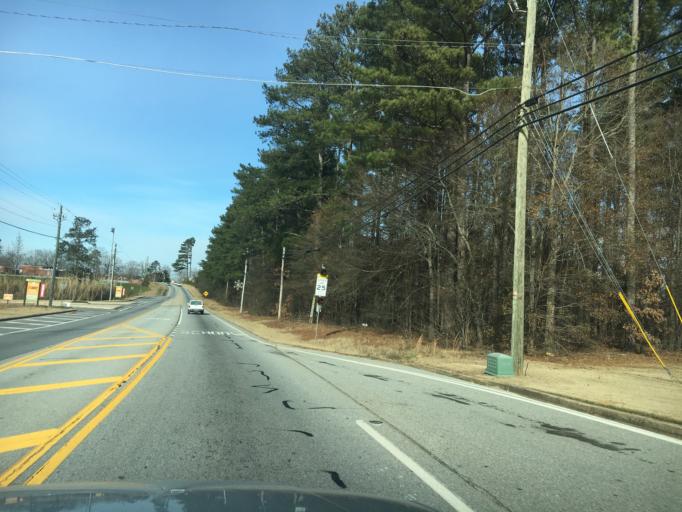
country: US
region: Georgia
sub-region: Jackson County
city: Hoschton
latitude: 34.1015
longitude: -83.7618
